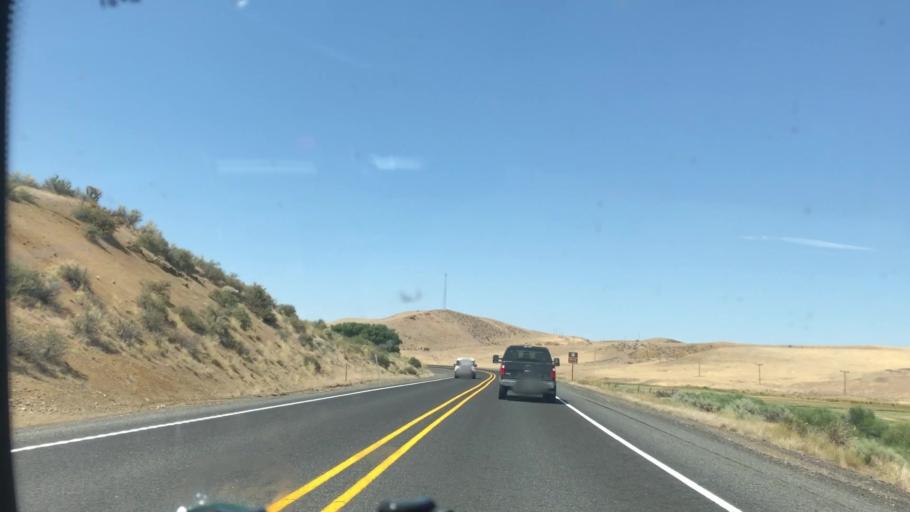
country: US
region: Idaho
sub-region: Owyhee County
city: Marsing
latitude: 43.2208
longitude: -117.0507
